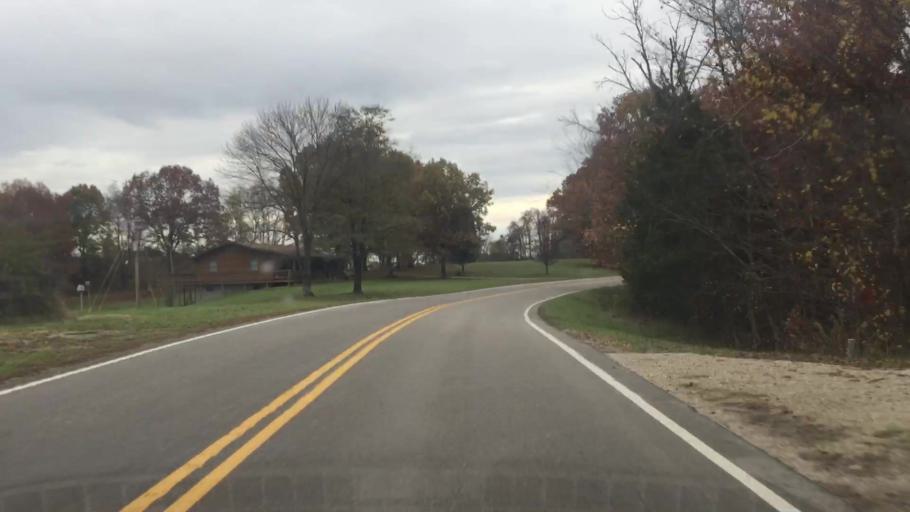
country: US
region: Missouri
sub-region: Gasconade County
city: Hermann
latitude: 38.7208
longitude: -91.7067
